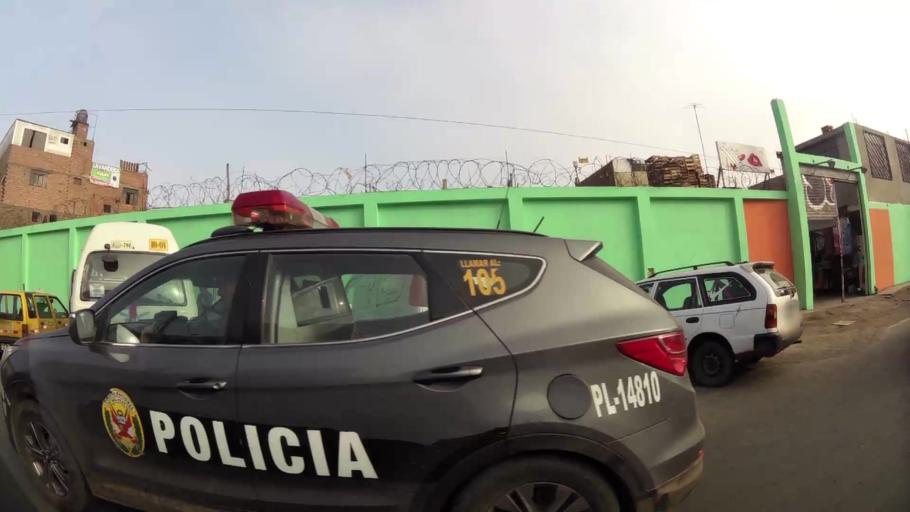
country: PE
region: Callao
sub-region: Callao
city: Callao
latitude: -12.0281
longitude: -77.0937
